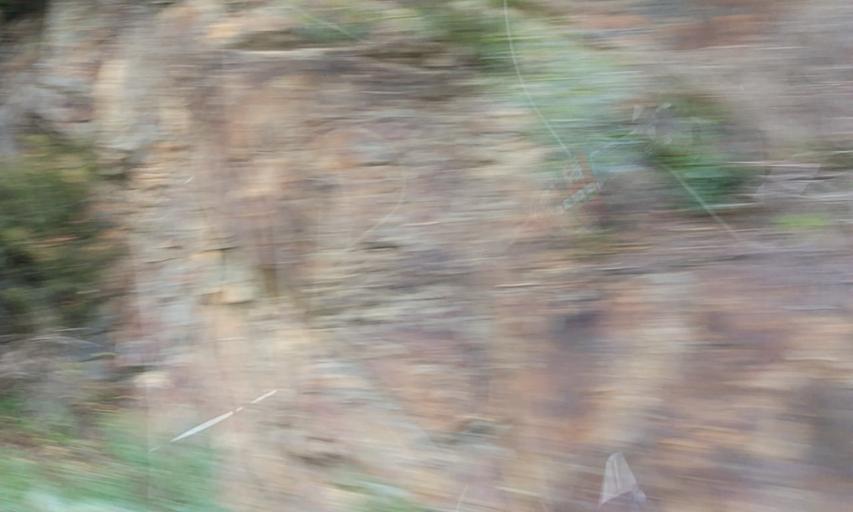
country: ES
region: Extremadura
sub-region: Provincia de Caceres
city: Acebo
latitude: 40.2252
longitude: -6.6768
